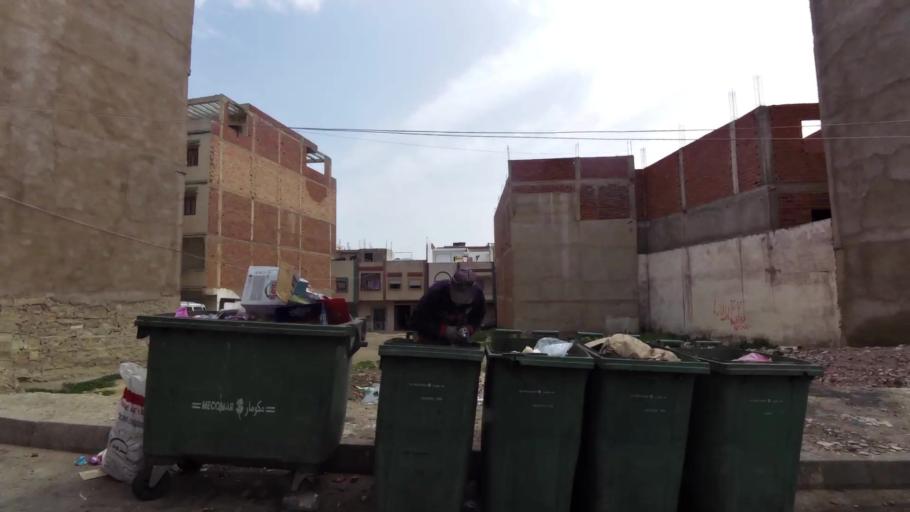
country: MA
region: Tanger-Tetouan
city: Tetouan
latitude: 35.5710
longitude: -5.3959
